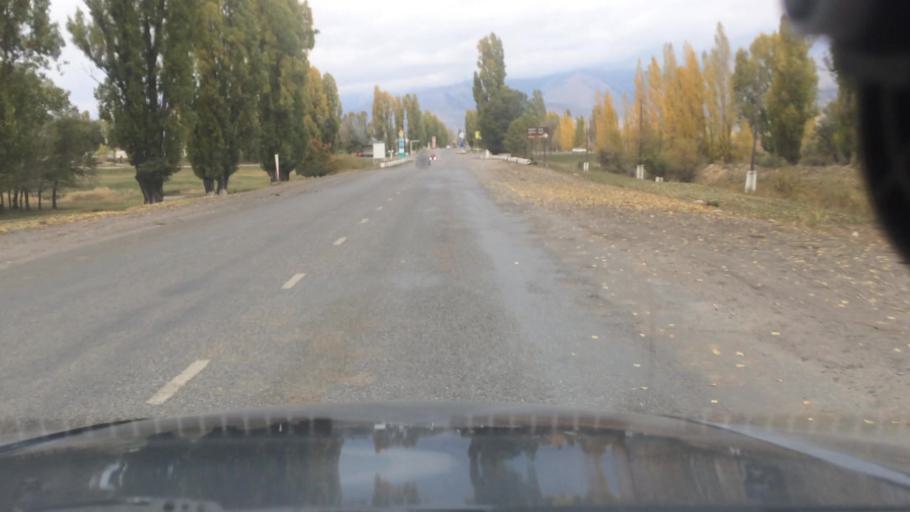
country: KG
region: Ysyk-Koel
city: Tyup
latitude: 42.7373
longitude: 78.3480
